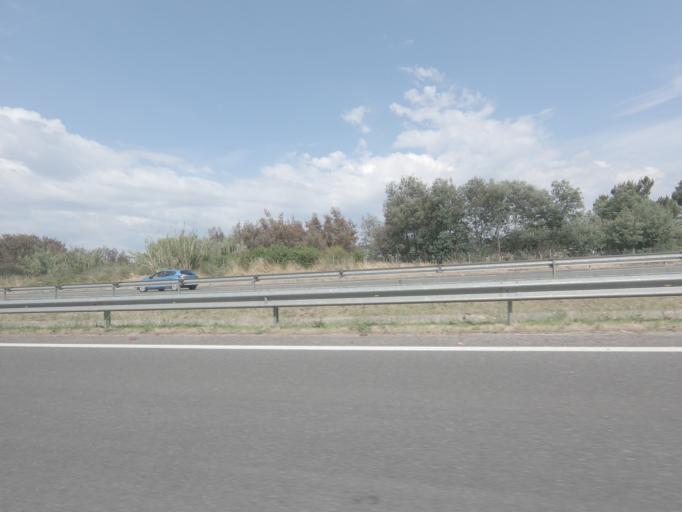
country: ES
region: Galicia
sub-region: Provincia de Ourense
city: Ourense
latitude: 42.3332
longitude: -7.8869
